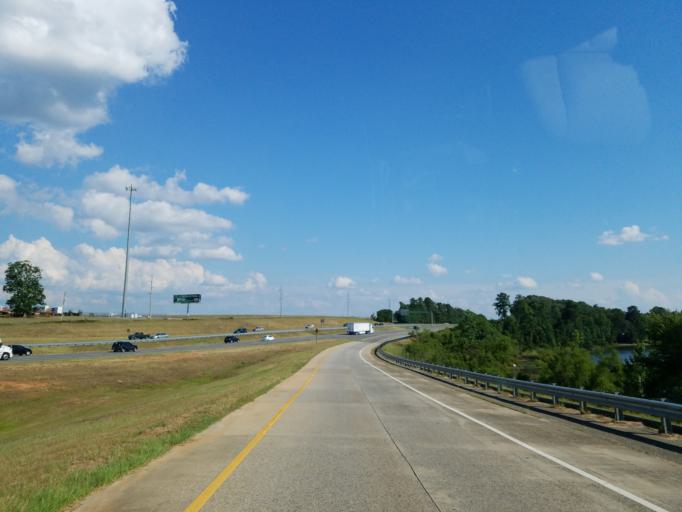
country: US
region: Georgia
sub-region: Houston County
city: Perry
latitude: 32.5439
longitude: -83.7448
